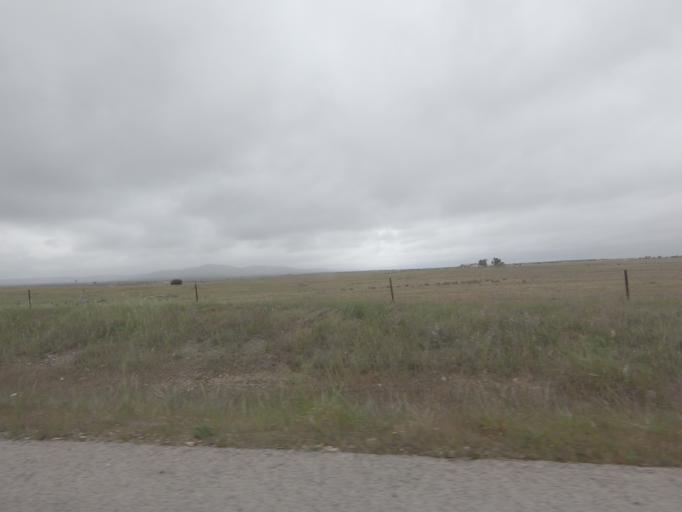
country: ES
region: Extremadura
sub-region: Provincia de Caceres
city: Malpartida de Caceres
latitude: 39.3509
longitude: -6.4695
